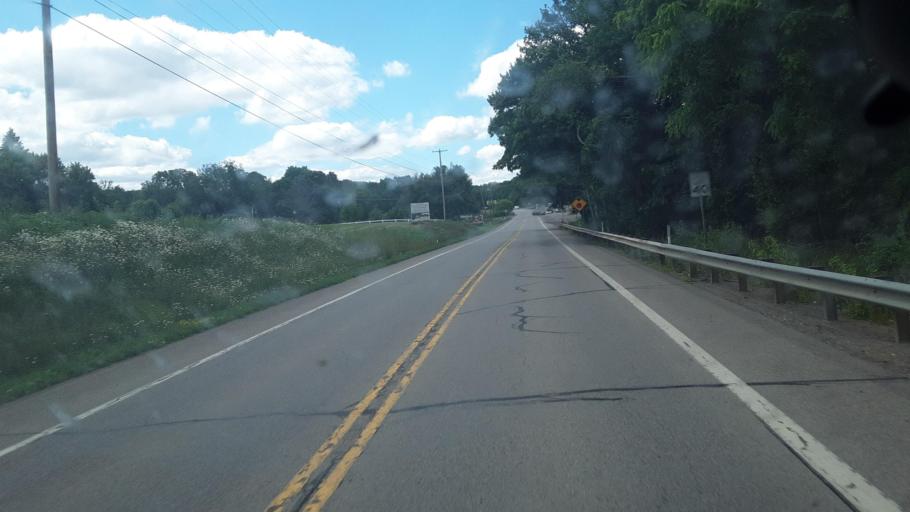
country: US
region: Pennsylvania
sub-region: Butler County
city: Slippery Rock
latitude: 41.0204
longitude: -80.1853
